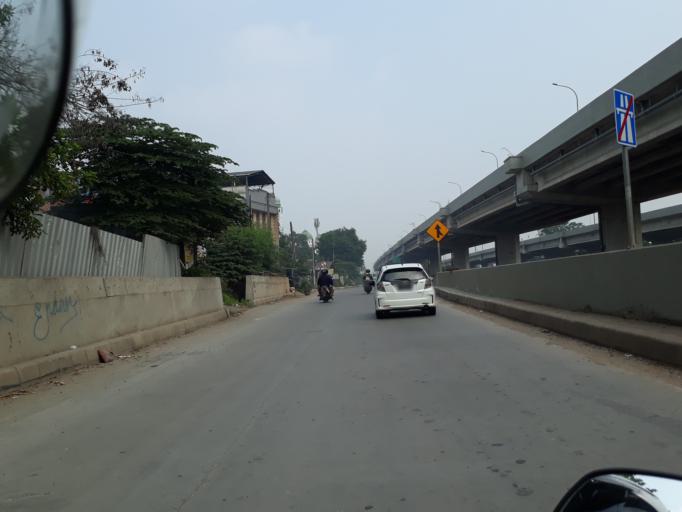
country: ID
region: West Java
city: Bekasi
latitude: -6.2499
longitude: 106.9384
